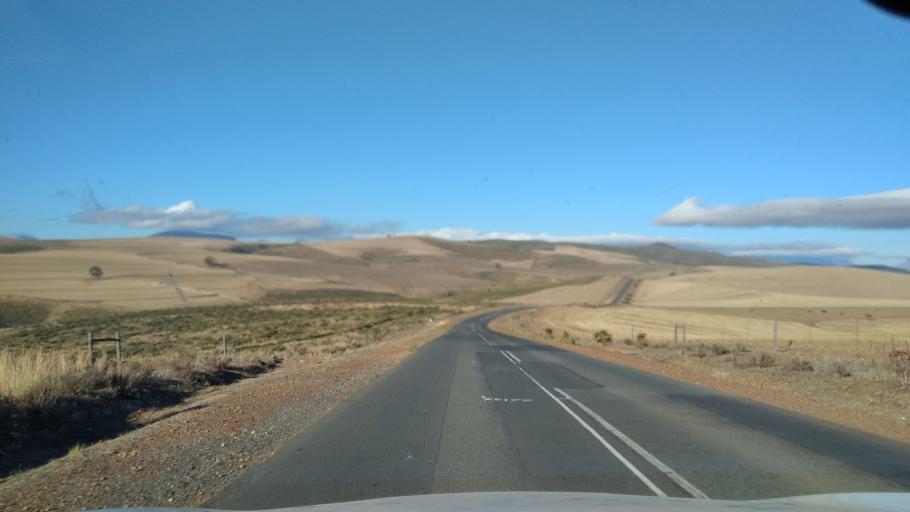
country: ZA
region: Western Cape
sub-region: Overberg District Municipality
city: Caledon
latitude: -34.1754
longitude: 19.2807
